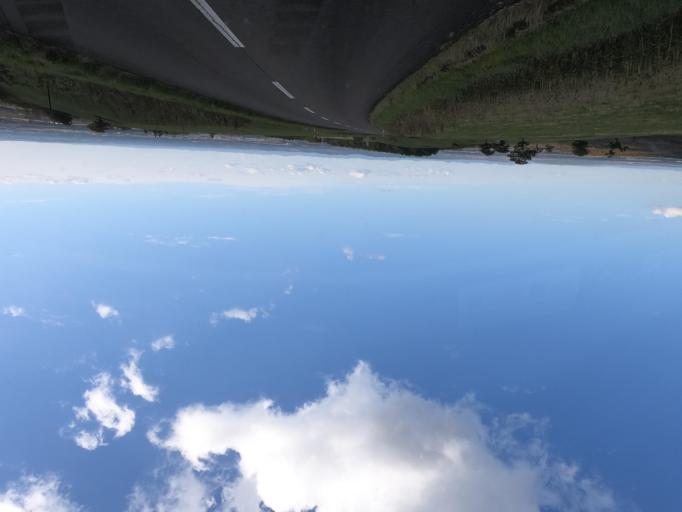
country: JP
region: Hokkaido
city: Otofuke
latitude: 43.2783
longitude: 143.2265
